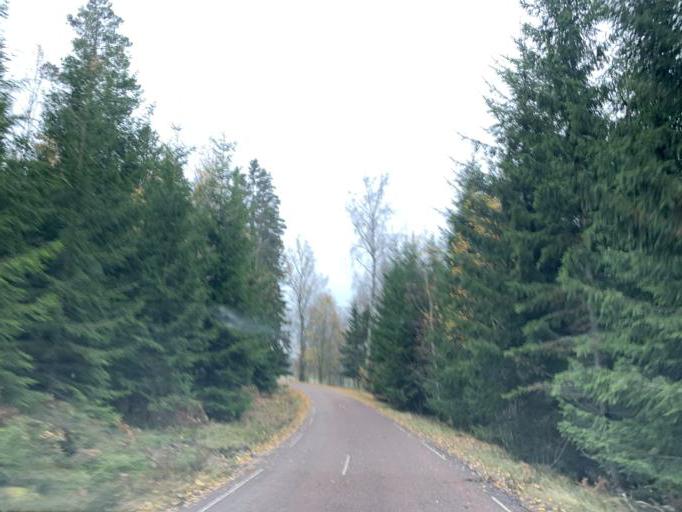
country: SE
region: Vaestmanland
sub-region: Surahammars Kommun
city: Surahammar
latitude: 59.6547
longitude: 16.0734
